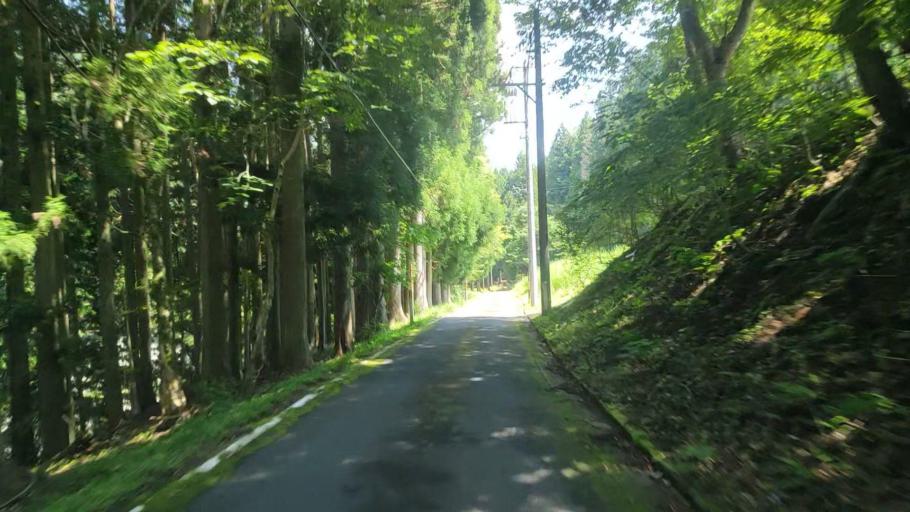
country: JP
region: Fukui
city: Ono
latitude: 35.7083
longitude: 136.5852
